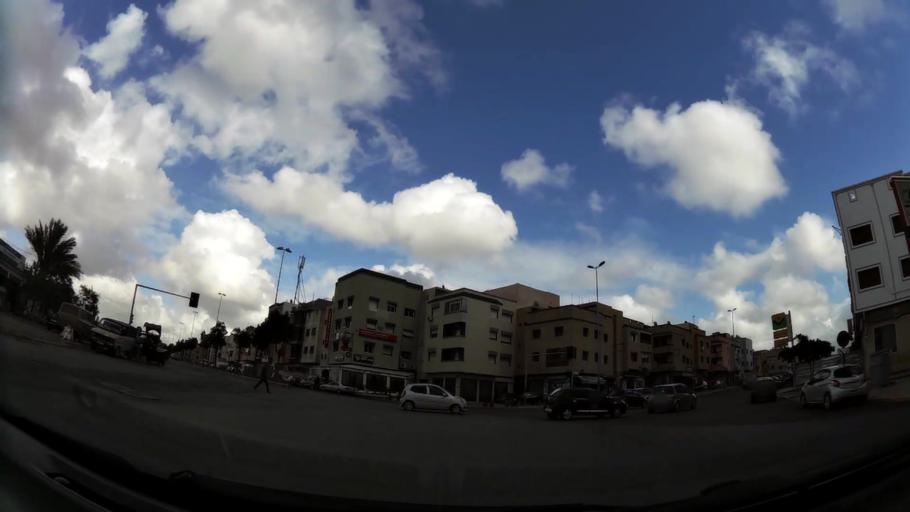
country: MA
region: Grand Casablanca
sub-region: Casablanca
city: Casablanca
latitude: 33.5466
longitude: -7.5955
